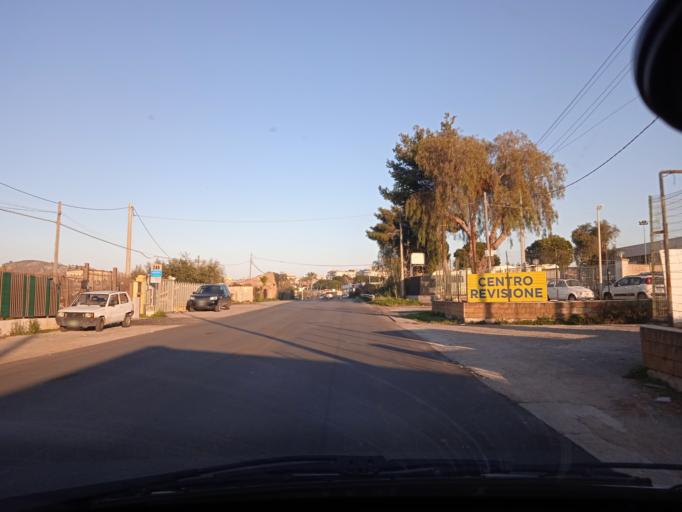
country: IT
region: Sicily
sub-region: Palermo
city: Bagheria
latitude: 38.0893
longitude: 13.4924
